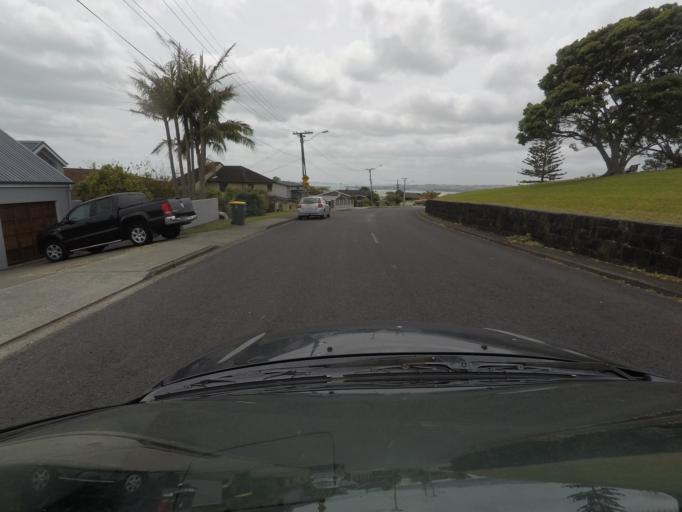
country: NZ
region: Auckland
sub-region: Auckland
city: Pakuranga
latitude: -36.8918
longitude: 174.9274
